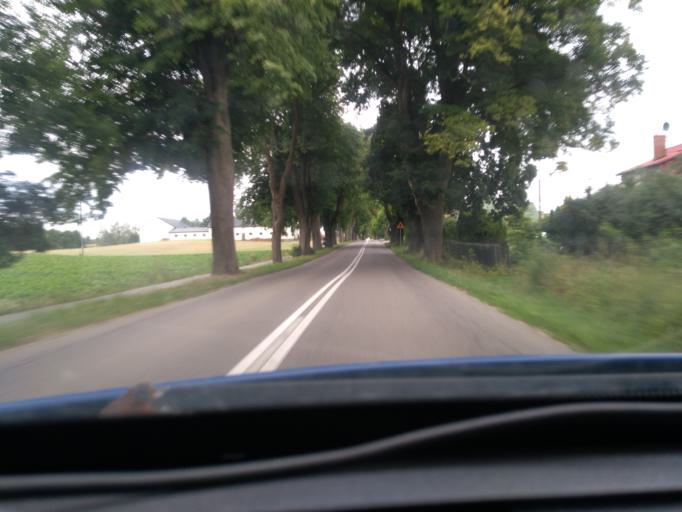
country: PL
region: Pomeranian Voivodeship
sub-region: Powiat kartuski
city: Zukowo
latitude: 54.3772
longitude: 18.3727
